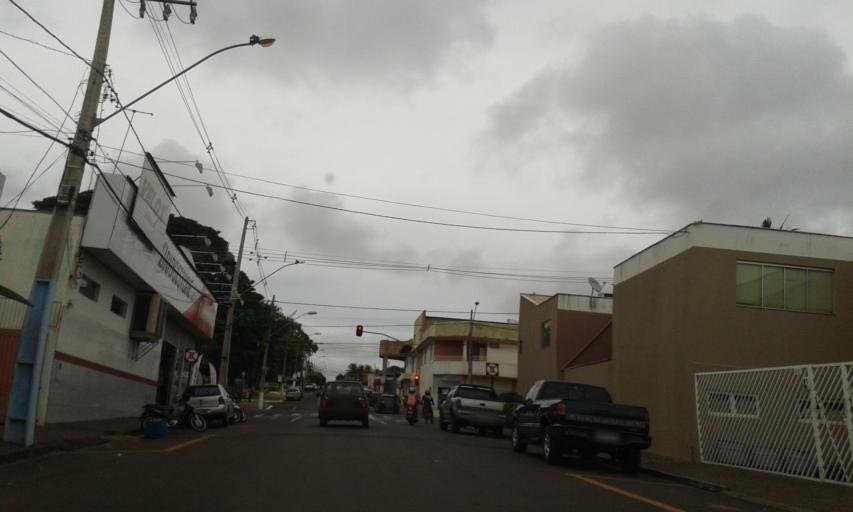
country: BR
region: Minas Gerais
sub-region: Ituiutaba
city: Ituiutaba
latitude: -18.9733
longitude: -49.4560
